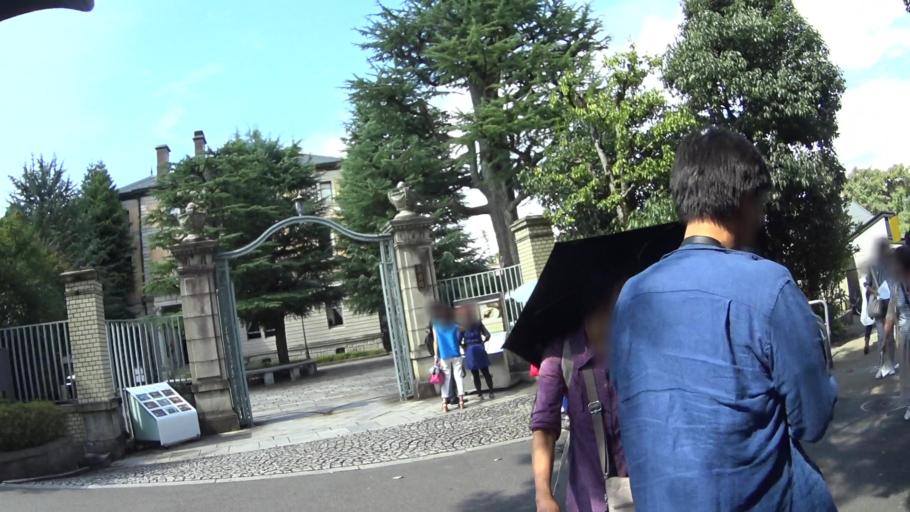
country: JP
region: Kyoto
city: Kyoto
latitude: 35.0032
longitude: 135.7807
